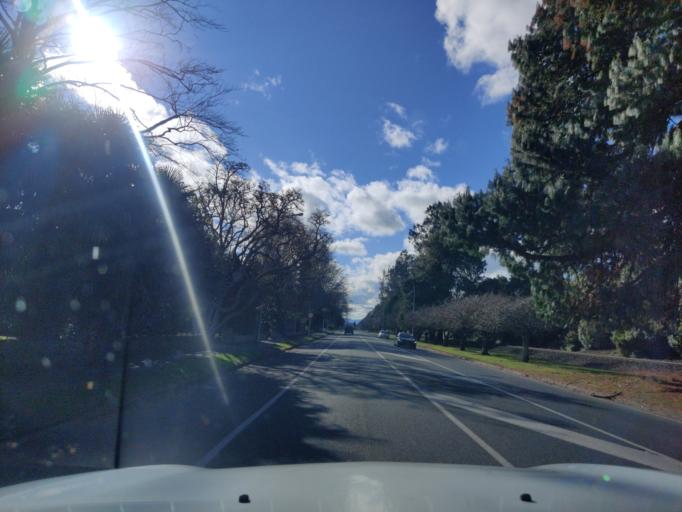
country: NZ
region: Waikato
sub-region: Matamata-Piako District
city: Matamata
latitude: -37.8201
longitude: 175.7711
